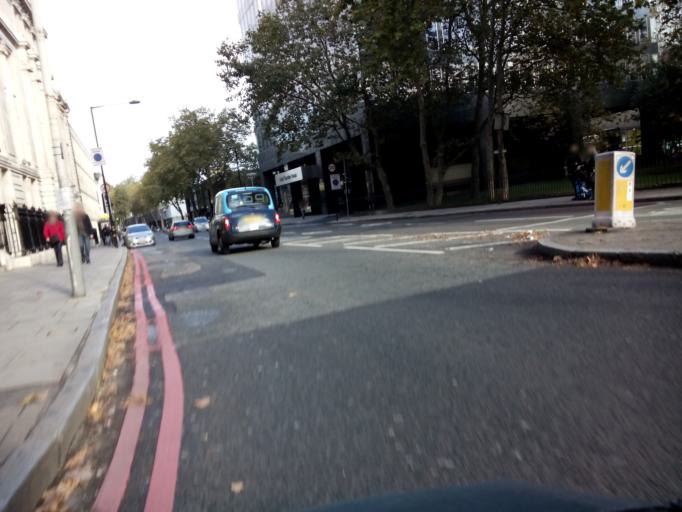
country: GB
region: England
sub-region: Greater London
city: Camden Town
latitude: 51.5264
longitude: -0.1338
